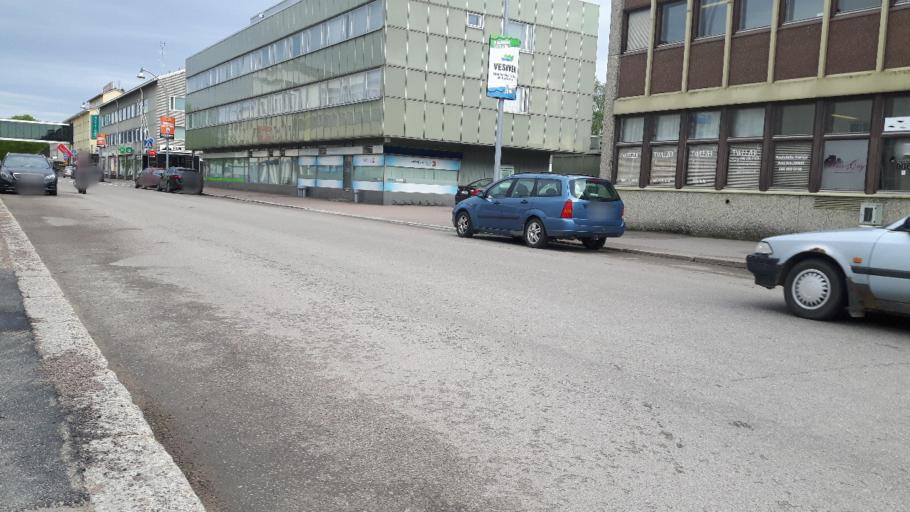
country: FI
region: Kymenlaakso
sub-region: Kotka-Hamina
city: Hamina
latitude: 60.5681
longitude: 27.1884
